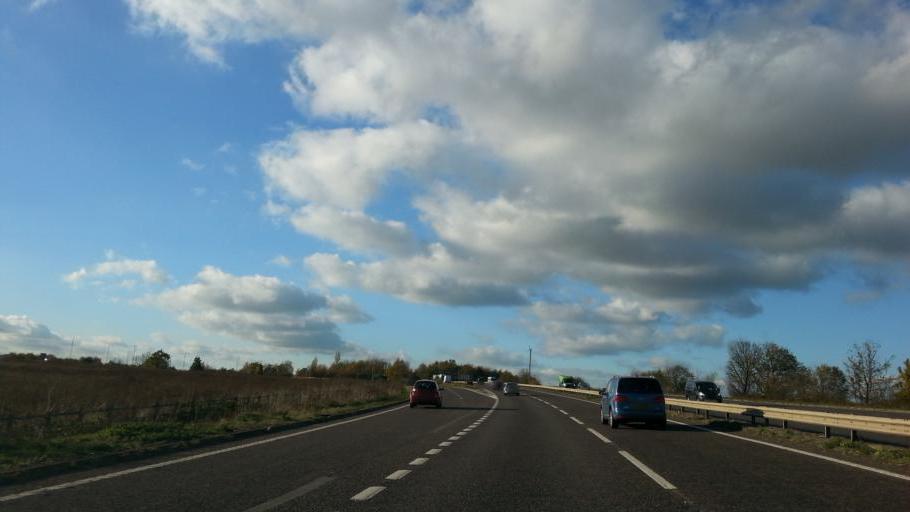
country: GB
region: England
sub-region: Suffolk
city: Bury St Edmunds
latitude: 52.2553
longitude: 0.6794
